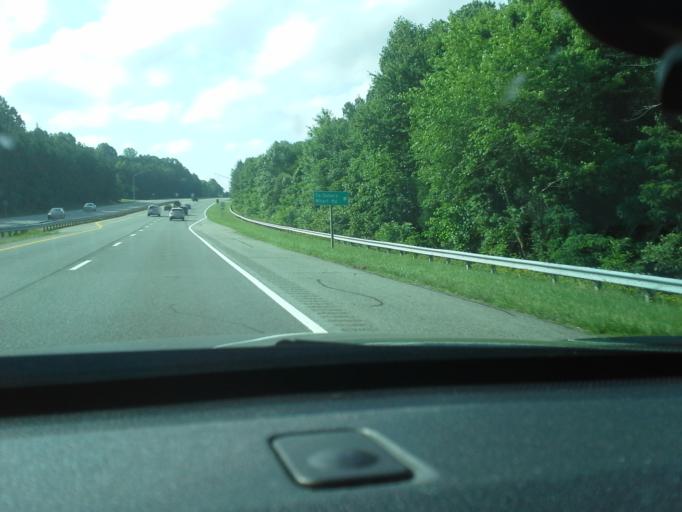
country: US
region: Maryland
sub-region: Calvert County
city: Lusby
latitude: 38.4191
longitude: -76.4590
